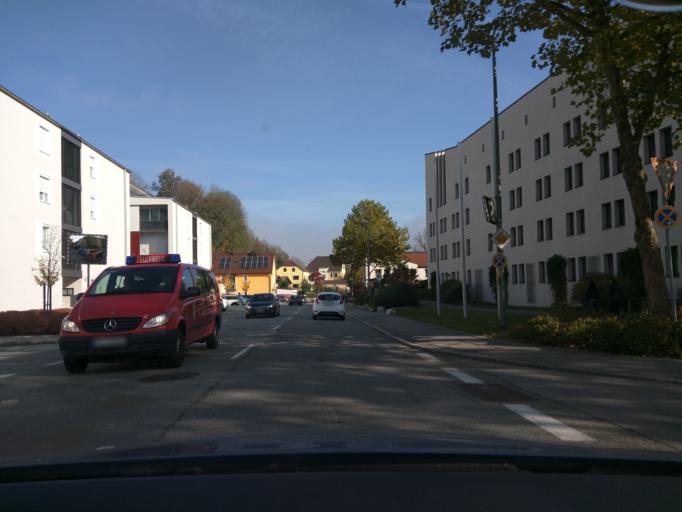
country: DE
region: Bavaria
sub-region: Lower Bavaria
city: Passau
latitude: 48.5669
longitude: 13.4493
